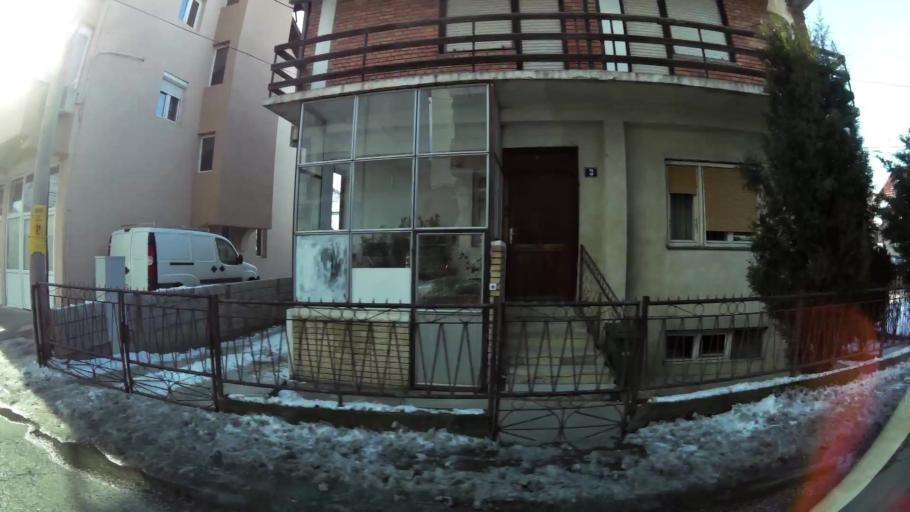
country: MK
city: Krushopek
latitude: 42.0072
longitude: 21.3581
